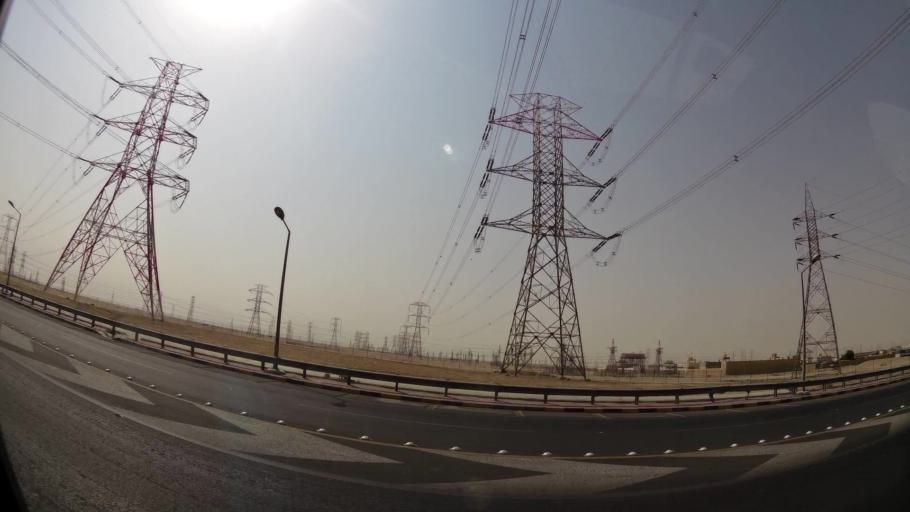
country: KW
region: Muhafazat al Jahra'
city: Al Jahra'
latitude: 29.3060
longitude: 47.6675
